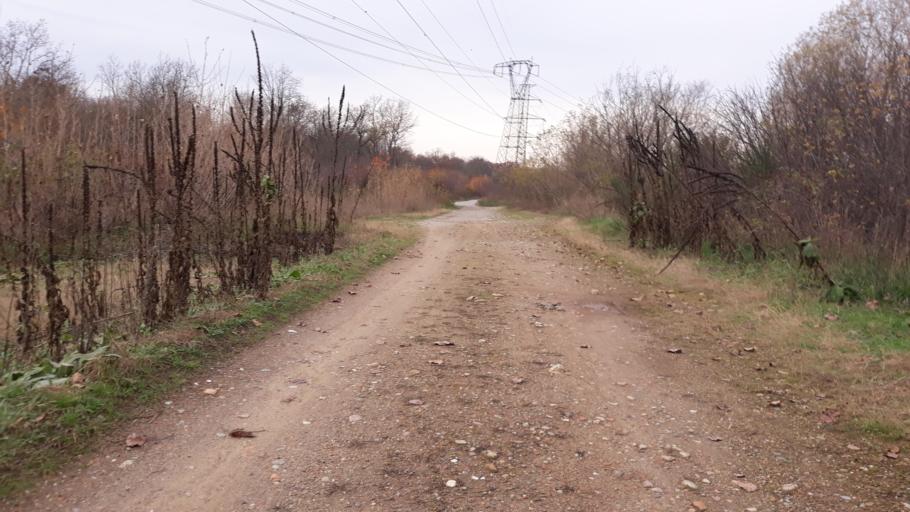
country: IT
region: Lombardy
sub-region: Citta metropolitana di Milano
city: Nosate
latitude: 45.5558
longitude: 8.7007
